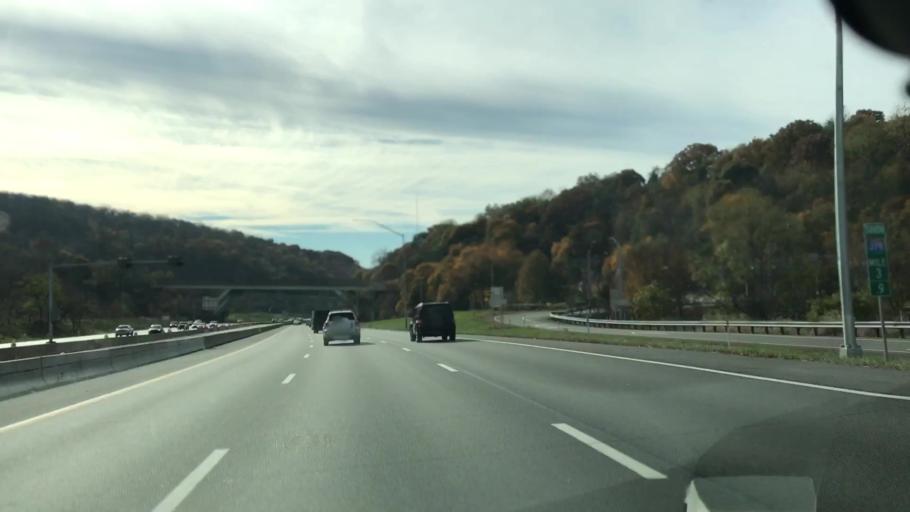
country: US
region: Pennsylvania
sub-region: Allegheny County
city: Millvale
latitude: 40.4864
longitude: -80.0091
